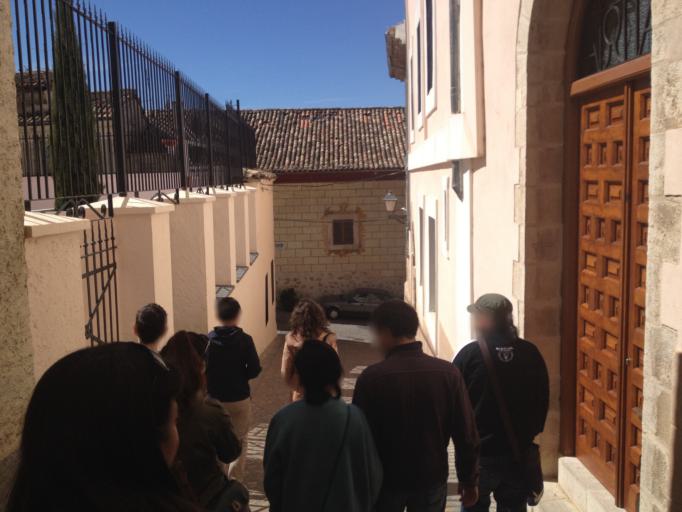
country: ES
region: Castille-La Mancha
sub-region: Provincia de Cuenca
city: Cuenca
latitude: 40.0750
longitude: -2.1337
